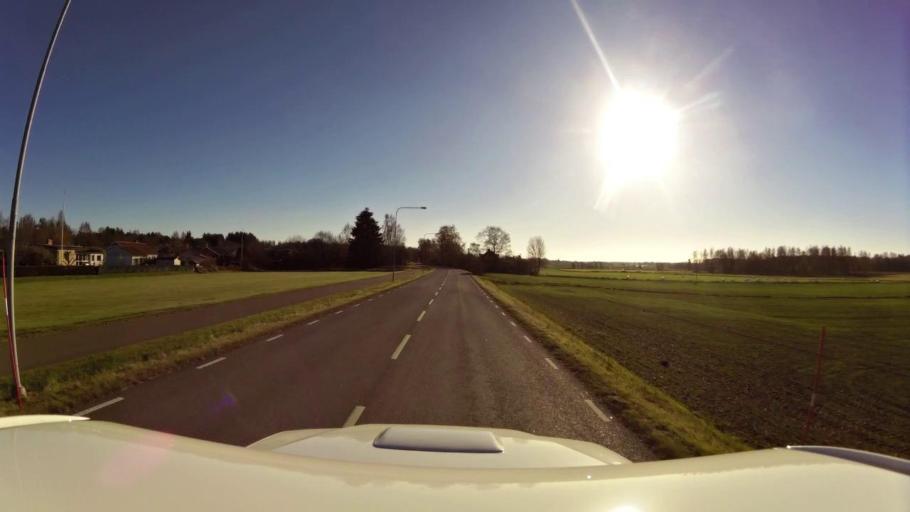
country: SE
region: OEstergoetland
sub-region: Linkopings Kommun
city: Malmslatt
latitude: 58.3641
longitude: 15.5606
